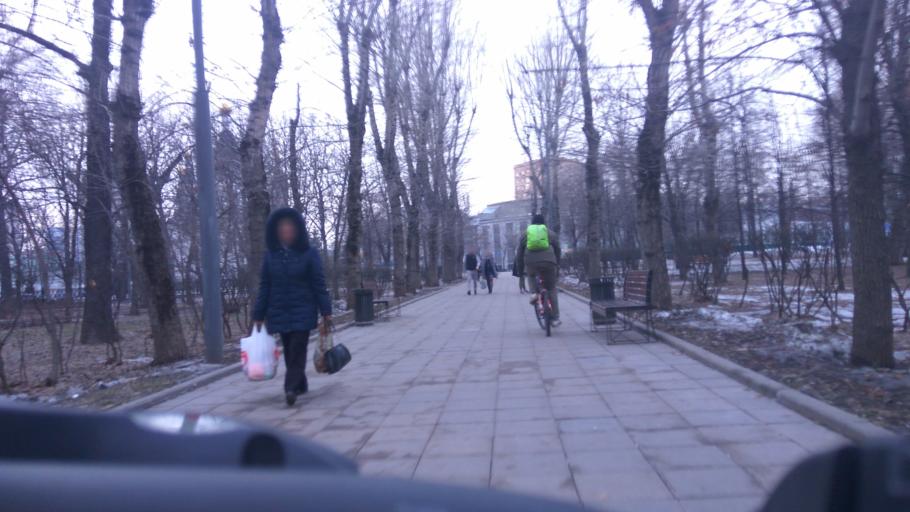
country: RU
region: Moskovskaya
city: Dorogomilovo
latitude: 55.7341
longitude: 37.5753
